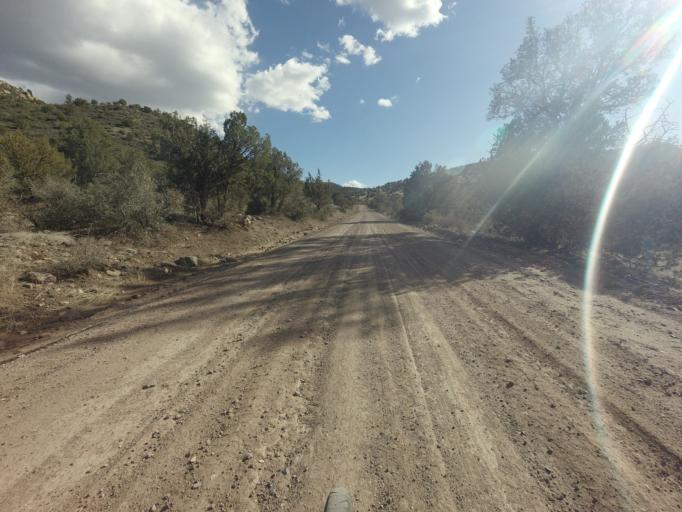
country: US
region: Arizona
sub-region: Yavapai County
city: Camp Verde
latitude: 34.4322
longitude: -111.6877
